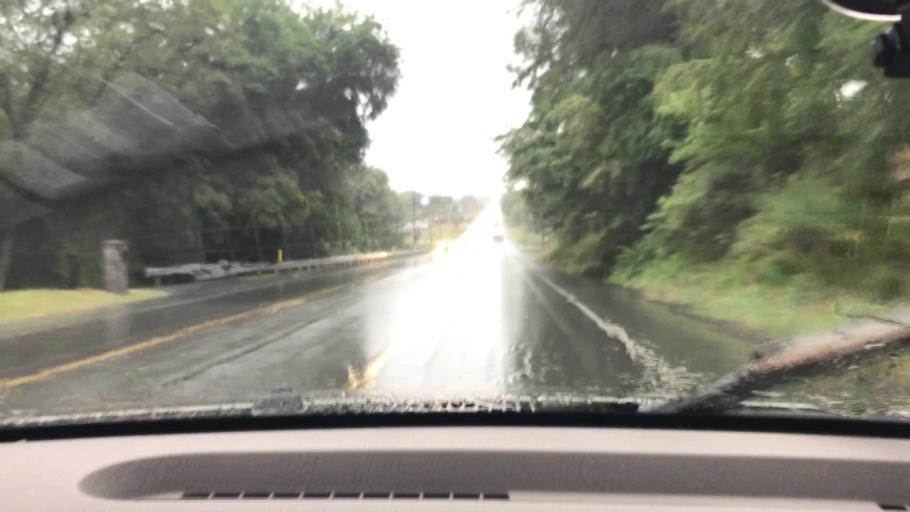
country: US
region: Pennsylvania
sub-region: Lancaster County
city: Rheems
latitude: 40.1356
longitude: -76.5773
